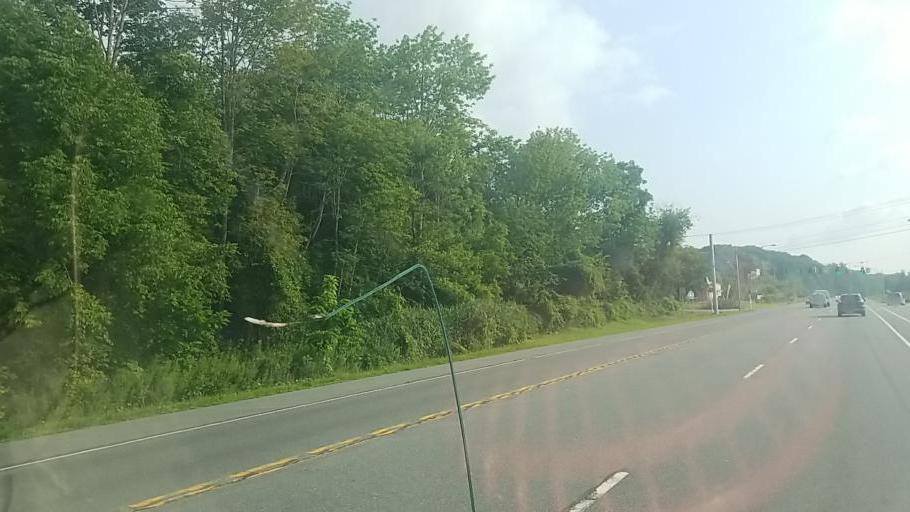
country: US
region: New York
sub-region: Fulton County
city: Gloversville
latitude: 43.0332
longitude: -74.3447
